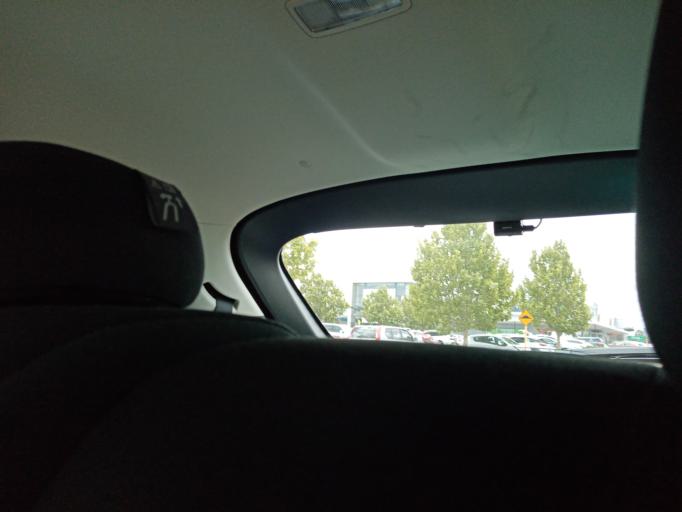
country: AU
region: Western Australia
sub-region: City of Cockburn
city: Success
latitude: -32.1335
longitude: 115.8563
